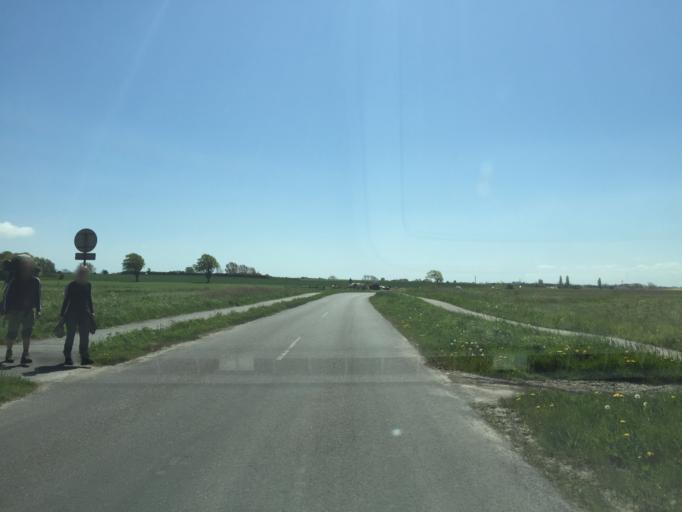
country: DK
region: Zealand
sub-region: Vordingborg Kommune
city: Stege
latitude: 55.0201
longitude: 12.2901
